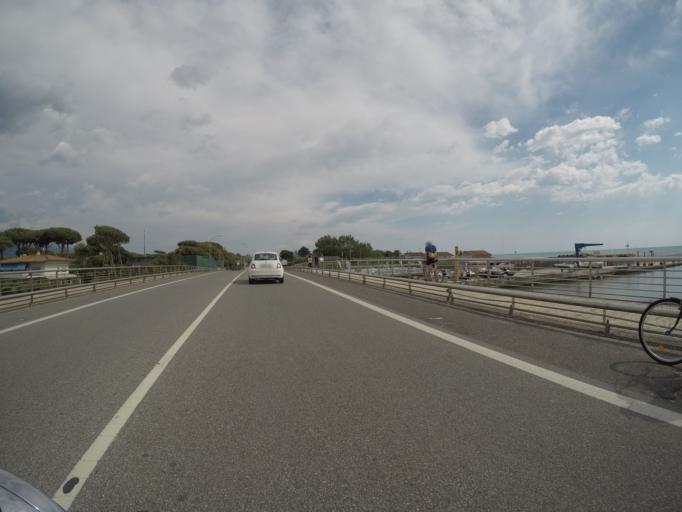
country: IT
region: Tuscany
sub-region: Provincia di Massa-Carrara
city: Capanne-Prato-Cinquale
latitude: 43.9785
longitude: 10.1428
